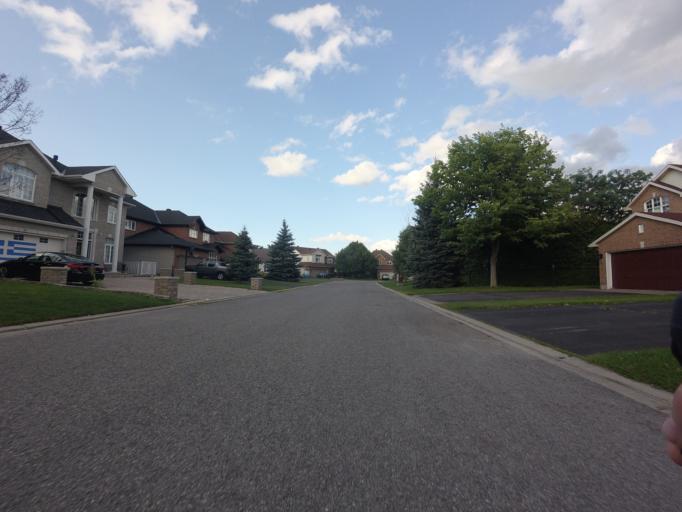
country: CA
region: Ontario
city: Bells Corners
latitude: 45.2868
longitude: -75.7117
